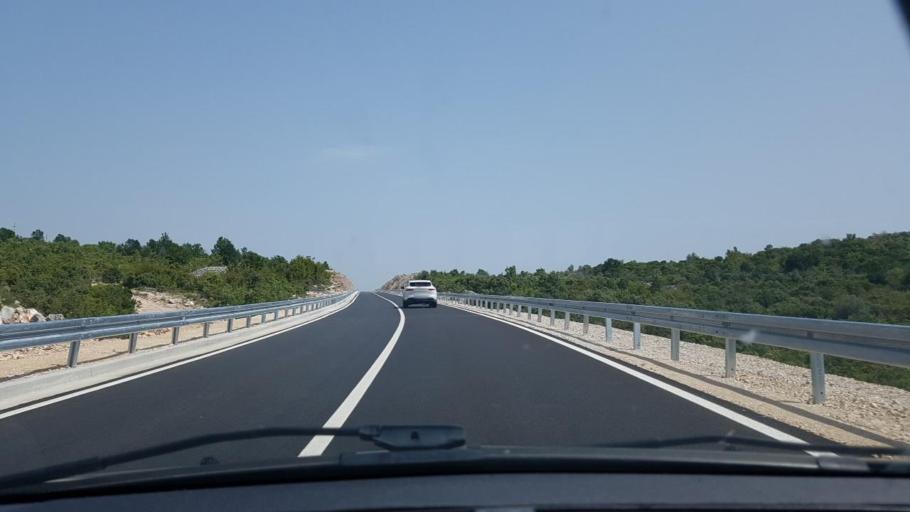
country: HR
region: Dubrovacko-Neretvanska
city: Podgora
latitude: 42.9479
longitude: 17.7614
